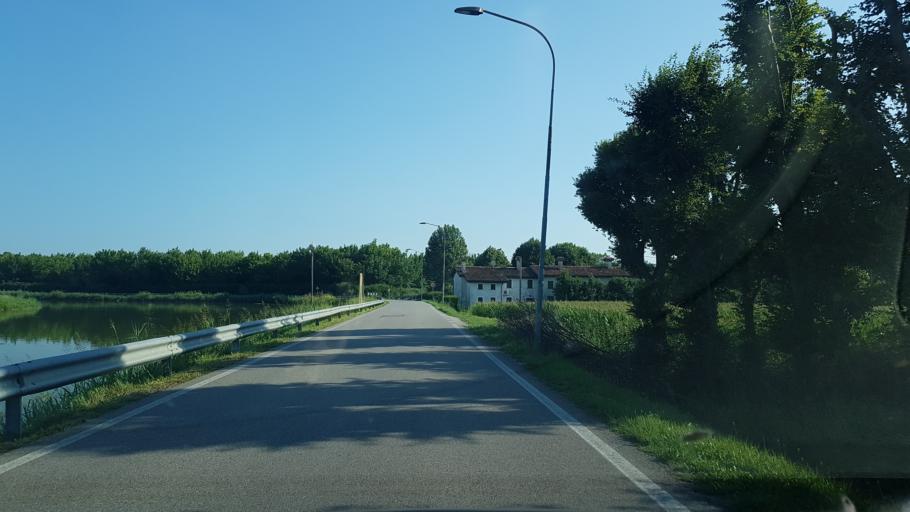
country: IT
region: Veneto
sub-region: Provincia di Venezia
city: San Giorgio di Livenza
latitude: 45.6417
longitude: 12.7903
